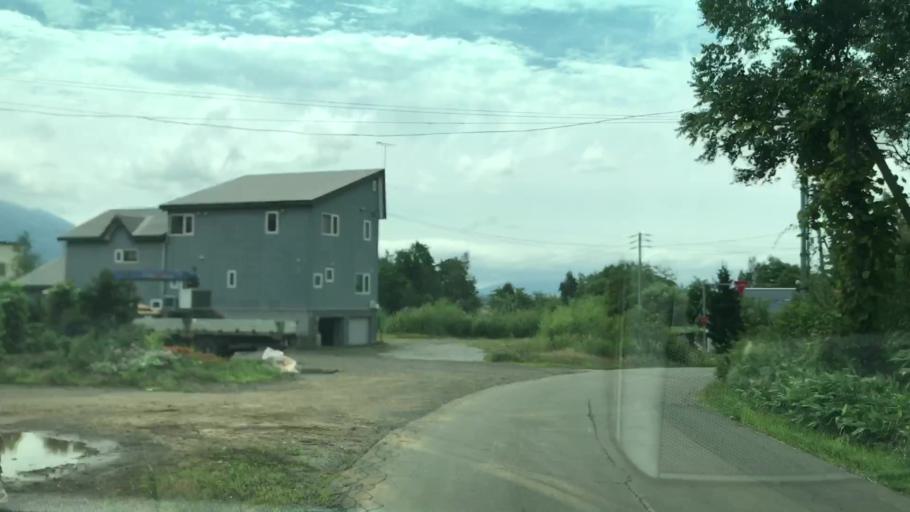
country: JP
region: Hokkaido
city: Niseko Town
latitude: 42.9134
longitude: 140.7528
